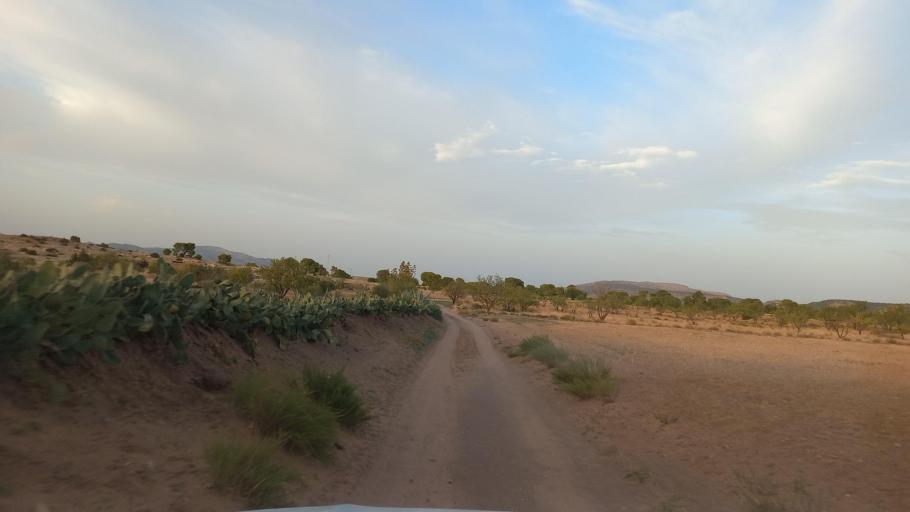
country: TN
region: Al Qasrayn
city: Sbiba
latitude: 35.4227
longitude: 8.9110
